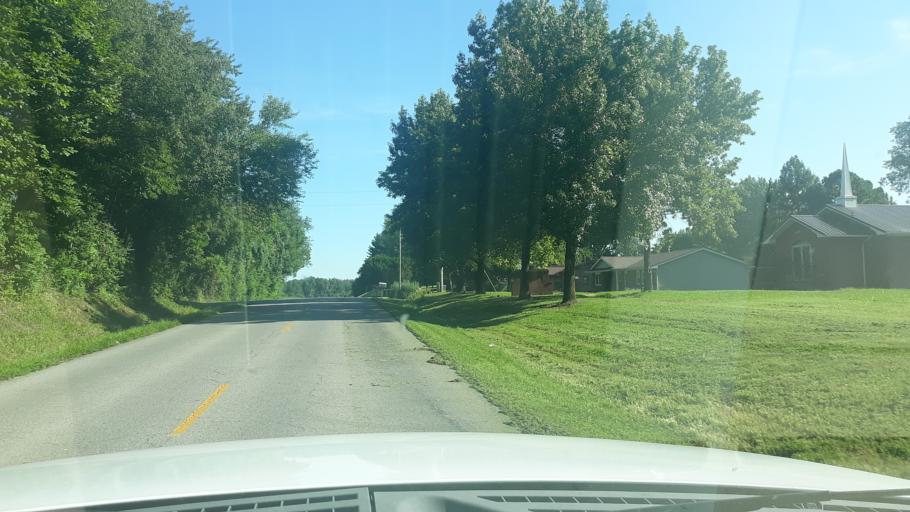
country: US
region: Illinois
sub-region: Saline County
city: Harrisburg
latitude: 37.7308
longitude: -88.5688
